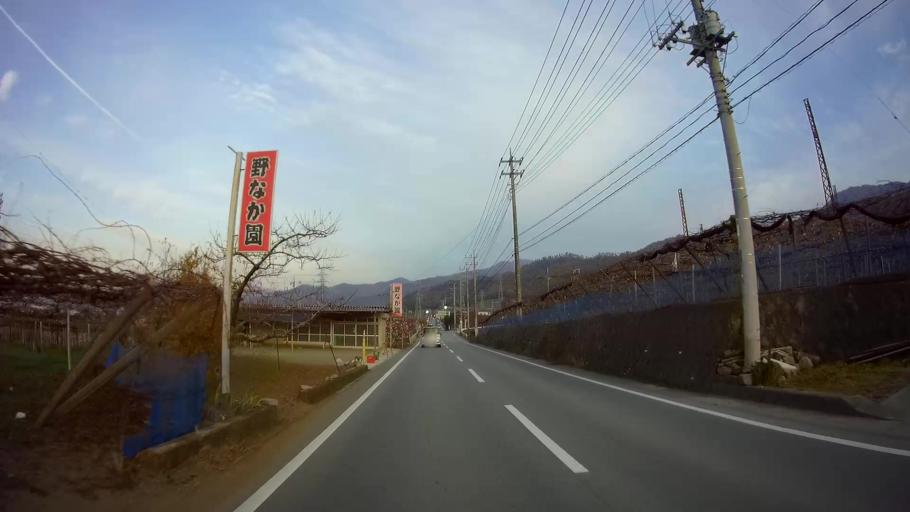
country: JP
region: Yamanashi
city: Isawa
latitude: 35.6128
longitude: 138.6640
